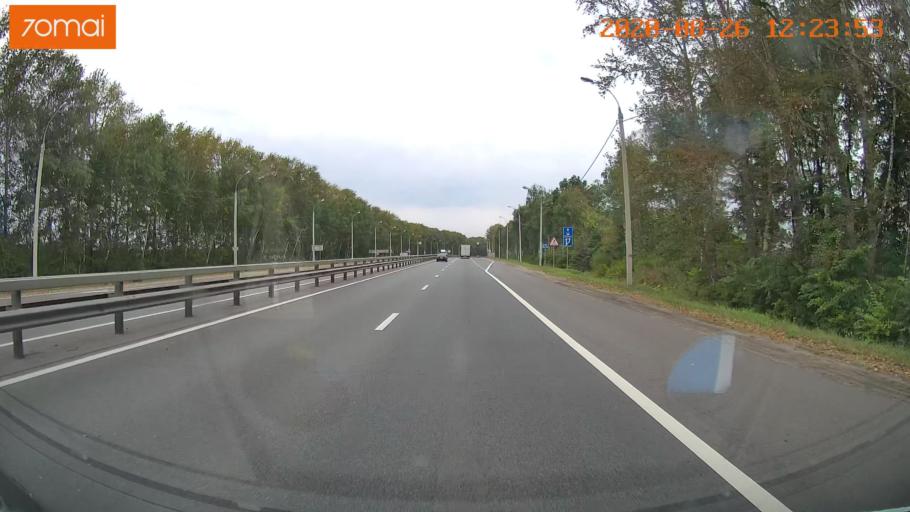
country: RU
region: Rjazan
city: Murmino
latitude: 54.5083
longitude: 39.9027
